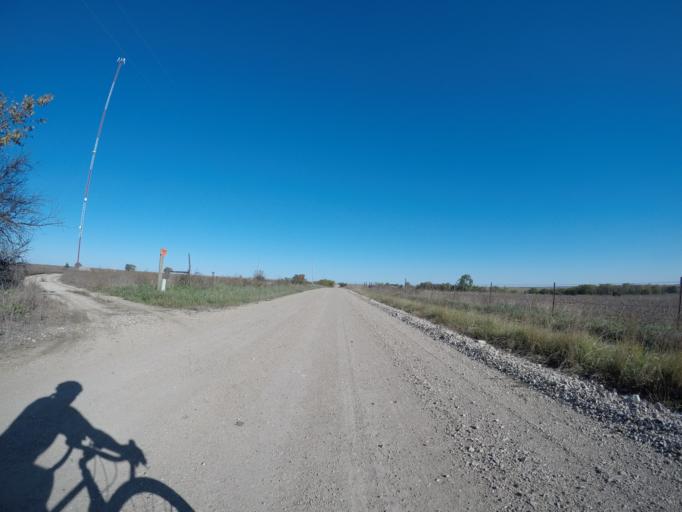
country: US
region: Kansas
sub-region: Wabaunsee County
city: Alma
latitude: 38.8590
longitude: -96.4098
